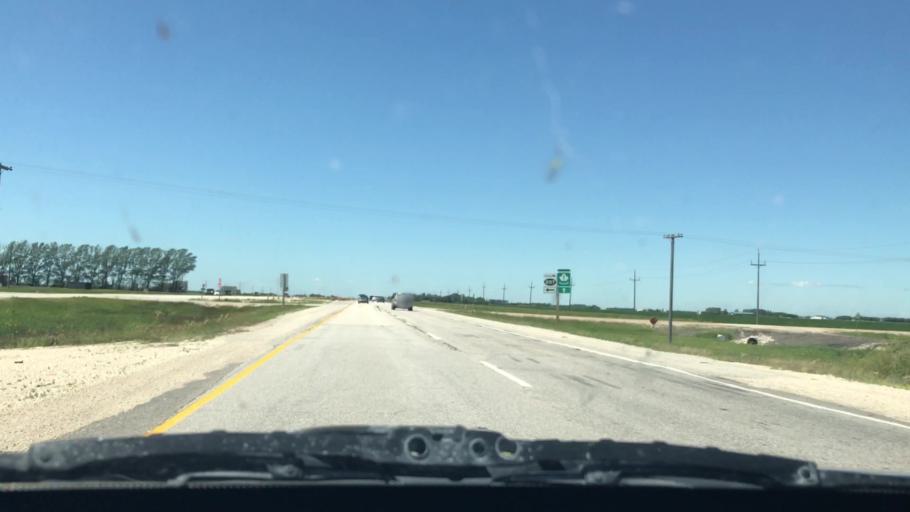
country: CA
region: Manitoba
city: Steinbach
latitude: 49.7332
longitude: -96.7262
